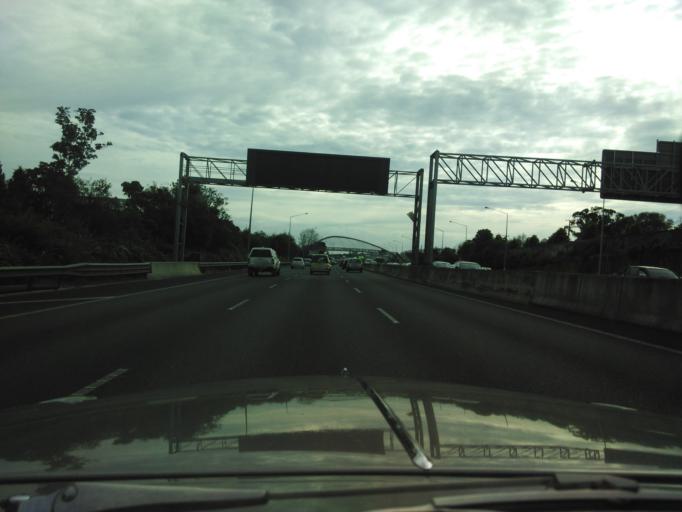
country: NZ
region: Auckland
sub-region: Auckland
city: Auckland
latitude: -36.8798
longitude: 174.7842
